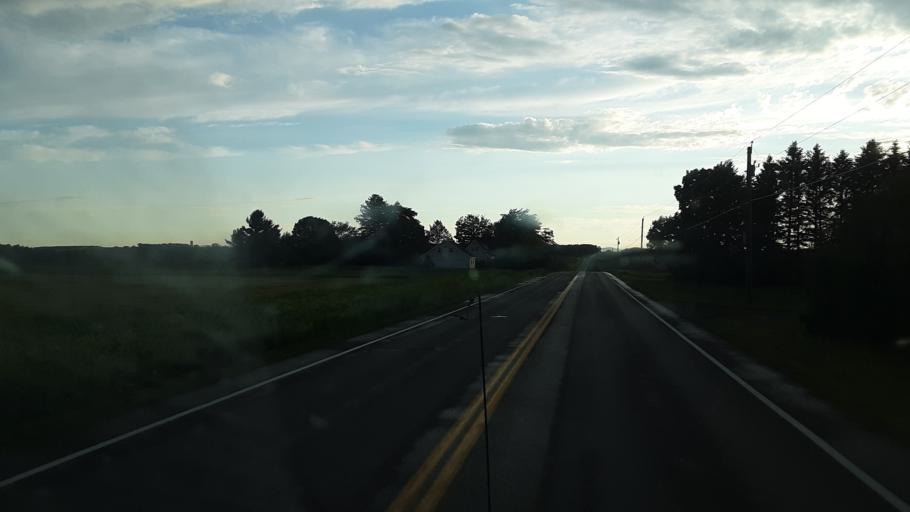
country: US
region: Maine
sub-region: Aroostook County
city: Presque Isle
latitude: 46.6752
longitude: -67.9593
